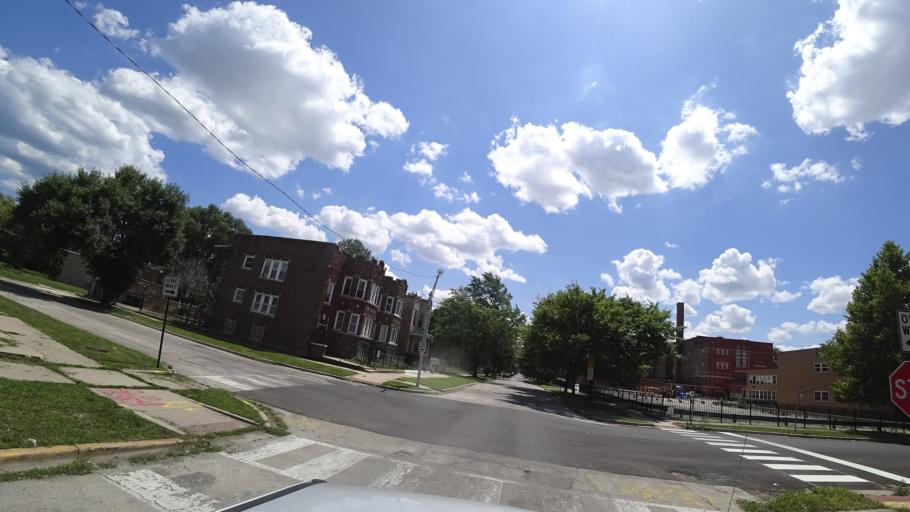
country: US
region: Illinois
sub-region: Cook County
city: Chicago
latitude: 41.7769
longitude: -87.6083
